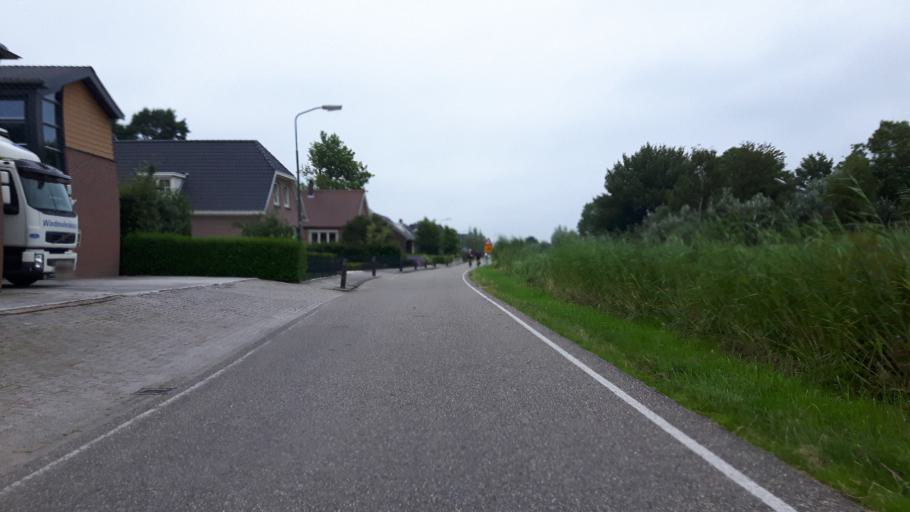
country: NL
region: Utrecht
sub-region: Gemeente Woerden
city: Woerden
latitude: 52.1155
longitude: 4.8940
